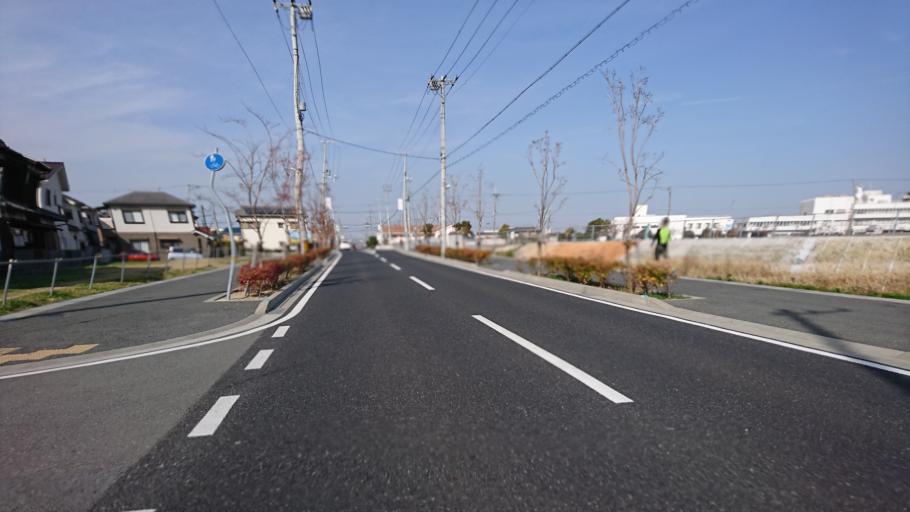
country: JP
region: Hyogo
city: Kakogawacho-honmachi
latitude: 34.7129
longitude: 134.8678
